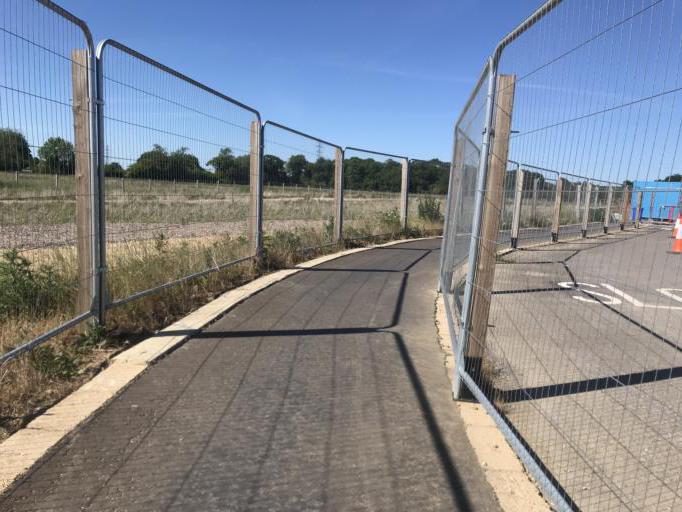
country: GB
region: England
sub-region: Cambridgeshire
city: Histon
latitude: 52.2304
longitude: 0.1075
